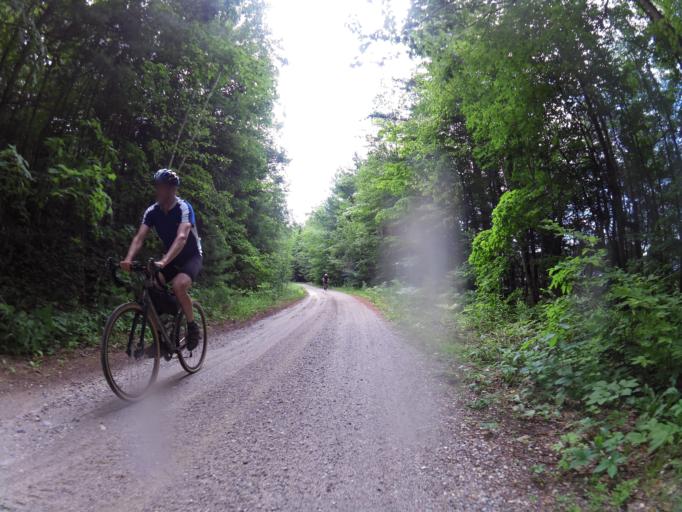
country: CA
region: Ontario
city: Perth
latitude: 45.0122
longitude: -76.5975
